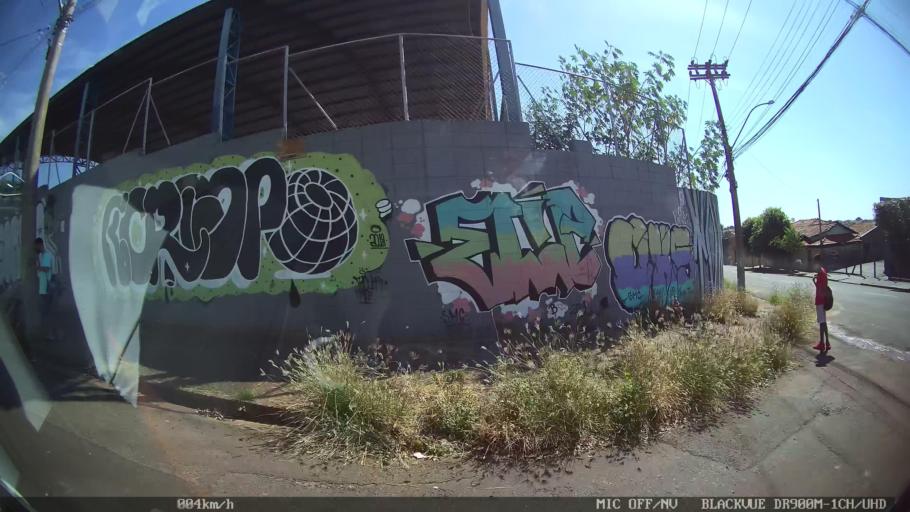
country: BR
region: Sao Paulo
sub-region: Sao Jose Do Rio Preto
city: Sao Jose do Rio Preto
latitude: -20.7755
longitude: -49.4025
